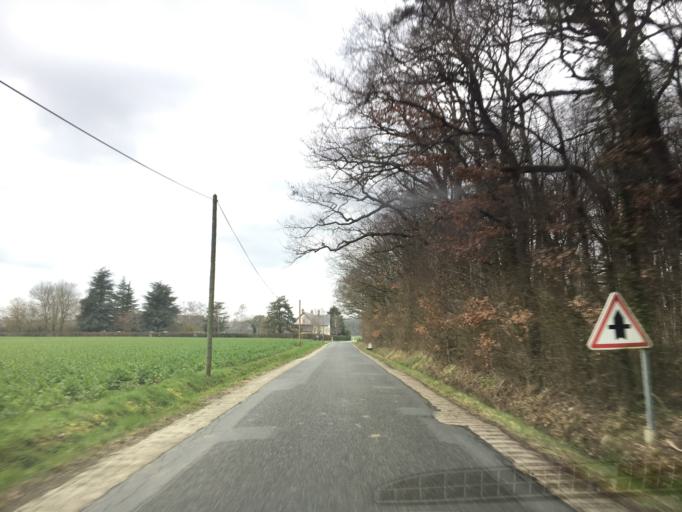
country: FR
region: Centre
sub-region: Departement d'Indre-et-Loire
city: Chanceaux-sur-Choisille
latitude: 47.4728
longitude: 0.7277
